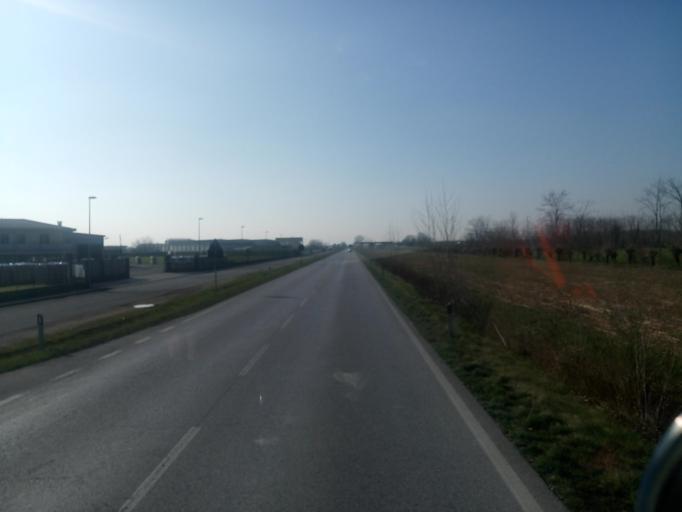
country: IT
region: Friuli Venezia Giulia
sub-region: Provincia di Udine
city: Mortegliano
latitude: 45.9303
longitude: 13.1520
